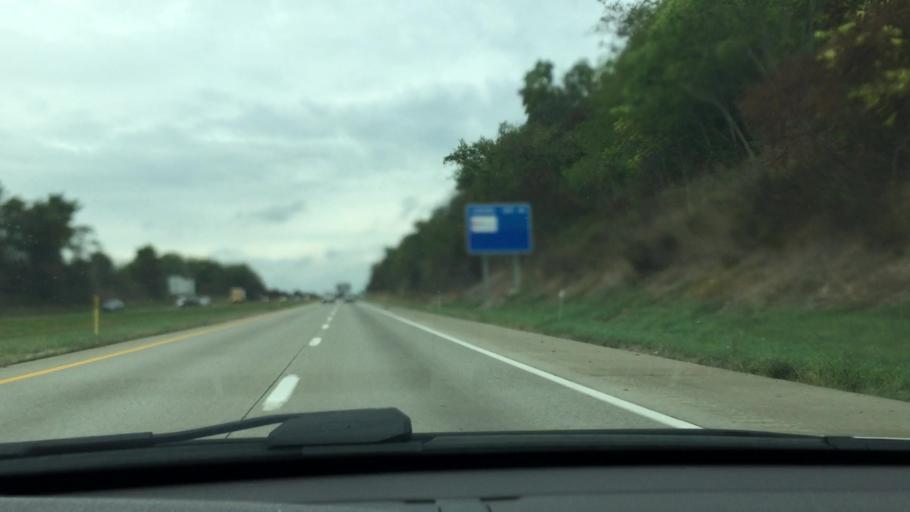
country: US
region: Pennsylvania
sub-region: Washington County
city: Canonsburg
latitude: 40.2831
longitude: -80.1641
